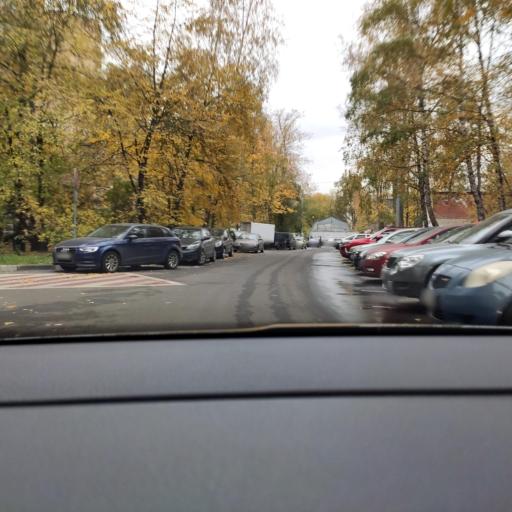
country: RU
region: Moscow
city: Vatutino
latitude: 55.8595
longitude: 37.6974
